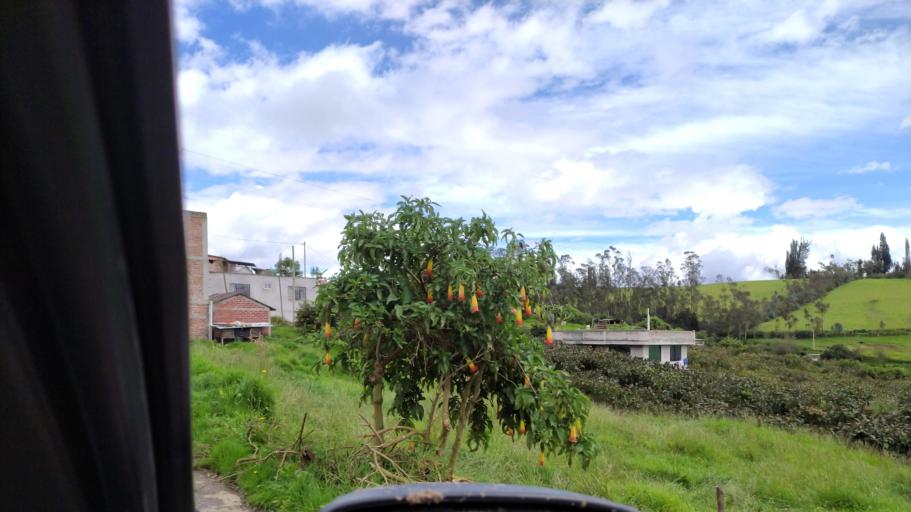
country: EC
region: Chimborazo
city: Riobamba
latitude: -1.6910
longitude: -78.5781
